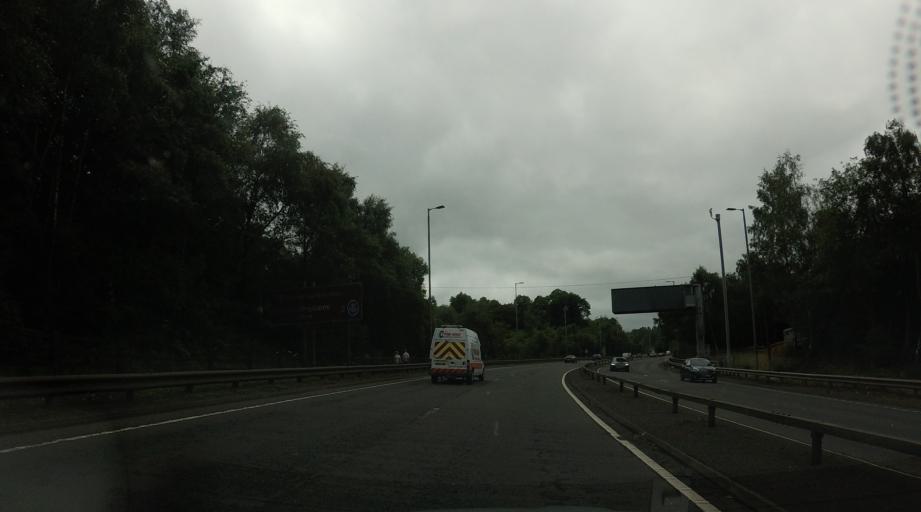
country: GB
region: Scotland
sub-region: South Lanarkshire
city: Bothwell
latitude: 55.7945
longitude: -4.0589
